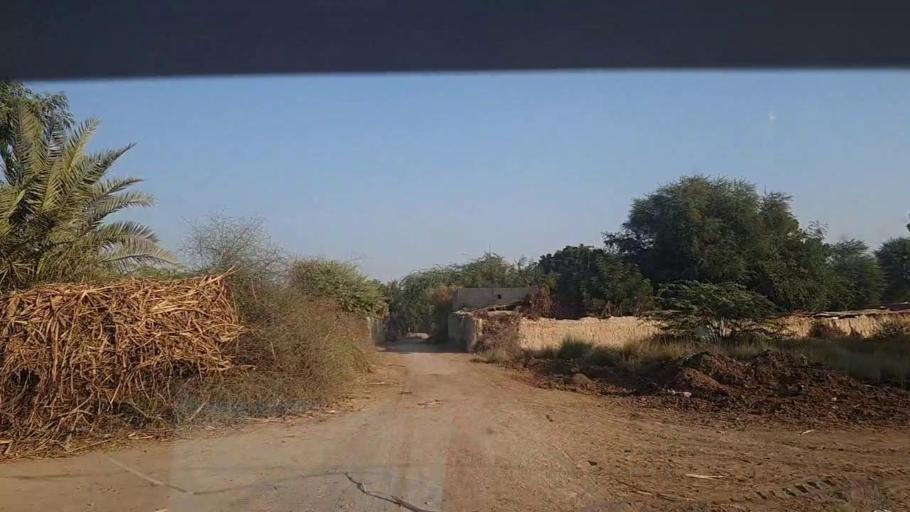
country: PK
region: Sindh
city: Sobhadero
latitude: 27.3048
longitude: 68.4244
